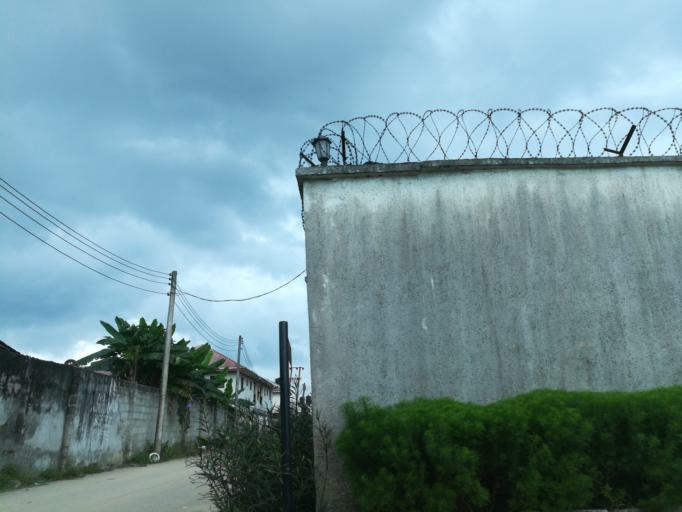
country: NG
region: Rivers
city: Port Harcourt
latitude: 4.8231
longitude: 7.0671
